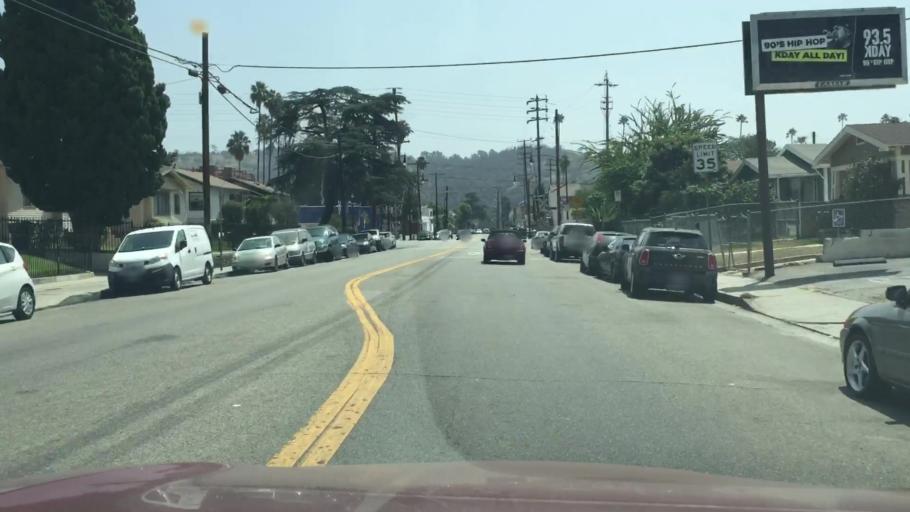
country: US
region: California
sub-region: Los Angeles County
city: South Pasadena
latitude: 34.1081
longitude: -118.2045
